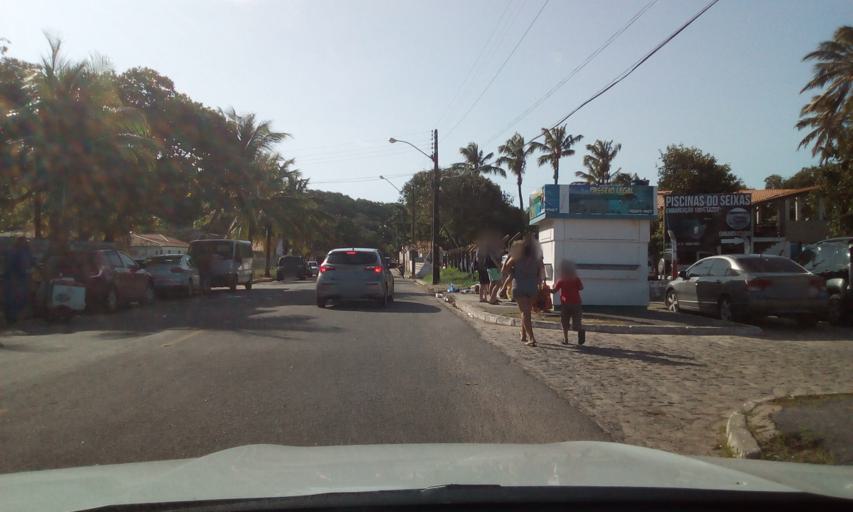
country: BR
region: Paraiba
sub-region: Joao Pessoa
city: Joao Pessoa
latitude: -7.1543
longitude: -34.7940
